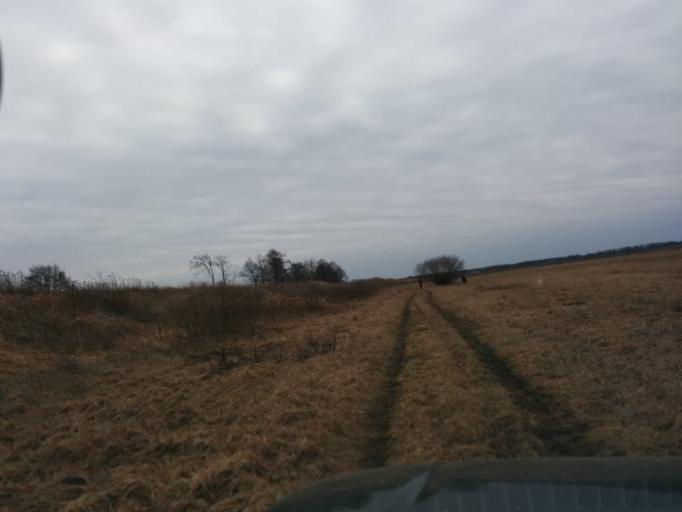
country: LV
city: Tireli
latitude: 56.9067
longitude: 23.6266
